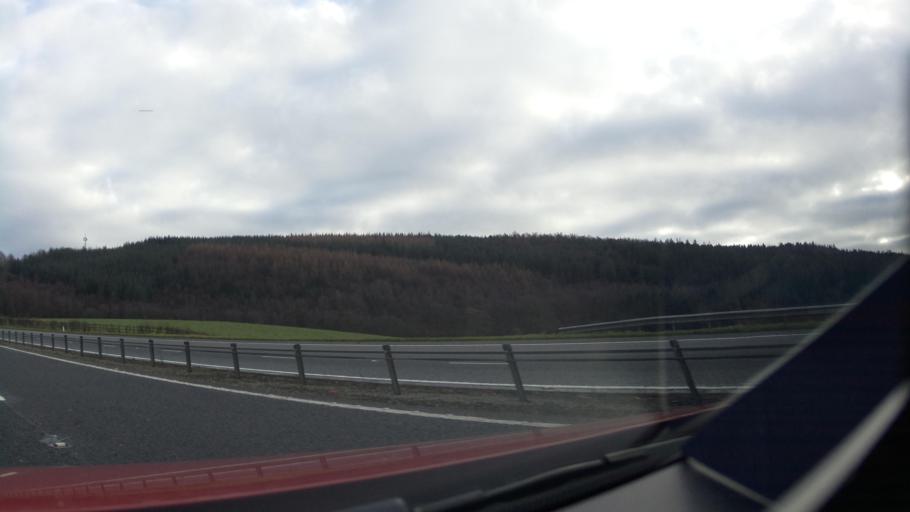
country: GB
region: Scotland
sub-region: Dumfries and Galloway
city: Annan
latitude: 55.0566
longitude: -3.2500
